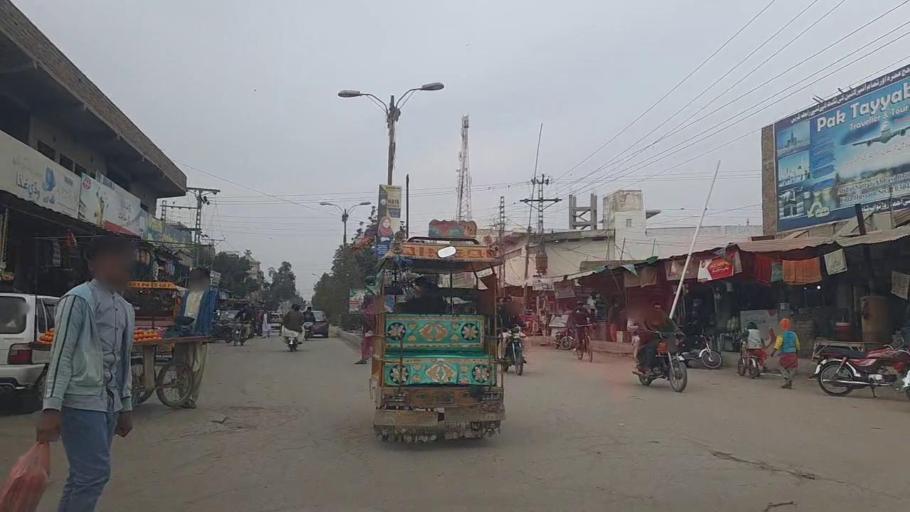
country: PK
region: Sindh
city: Nawabshah
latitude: 26.2541
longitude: 68.4031
